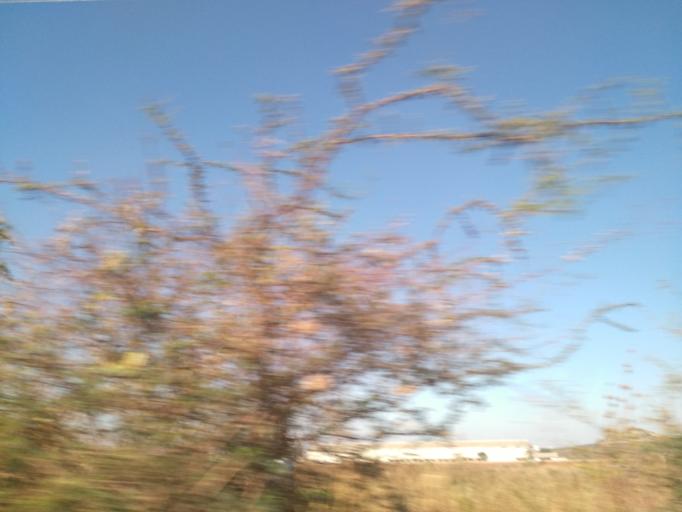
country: TZ
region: Dodoma
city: Dodoma
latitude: -6.1703
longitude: 35.7005
